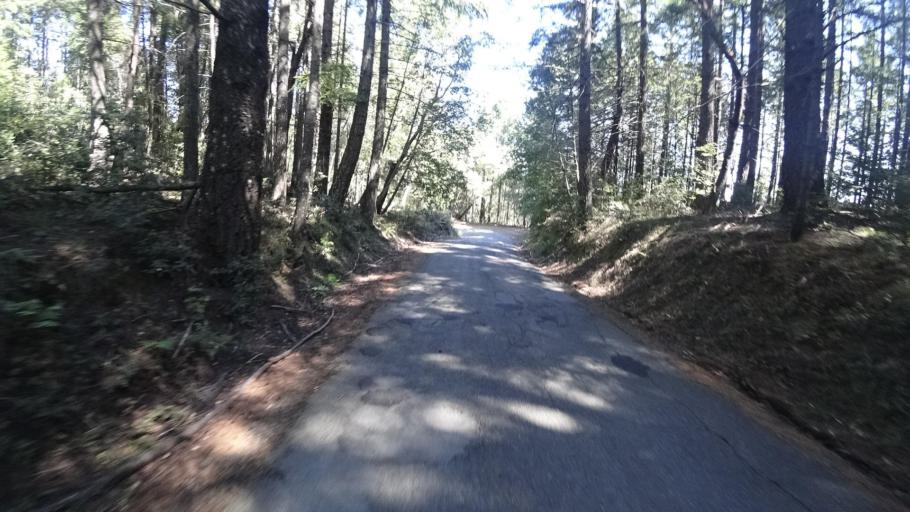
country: US
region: California
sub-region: Humboldt County
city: Redway
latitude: 40.1877
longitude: -124.0927
